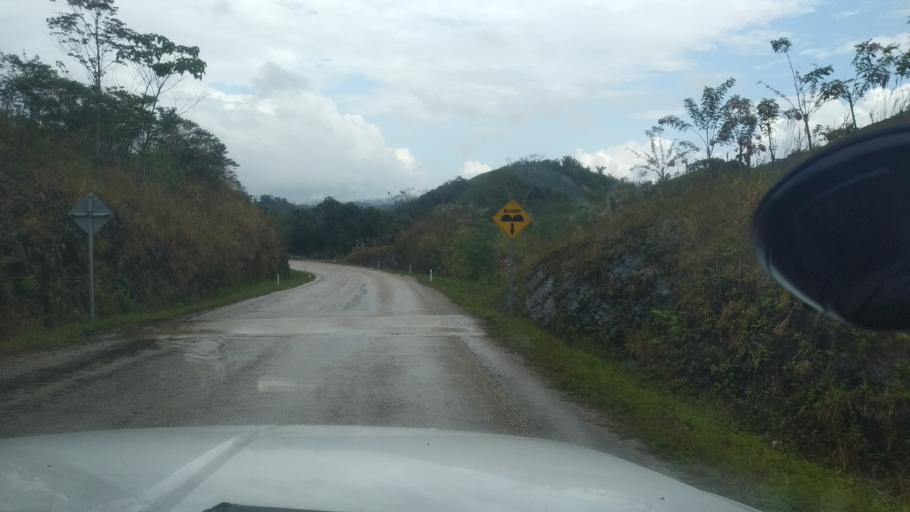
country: GT
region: Peten
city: San Luis
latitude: 16.1865
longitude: -89.1921
